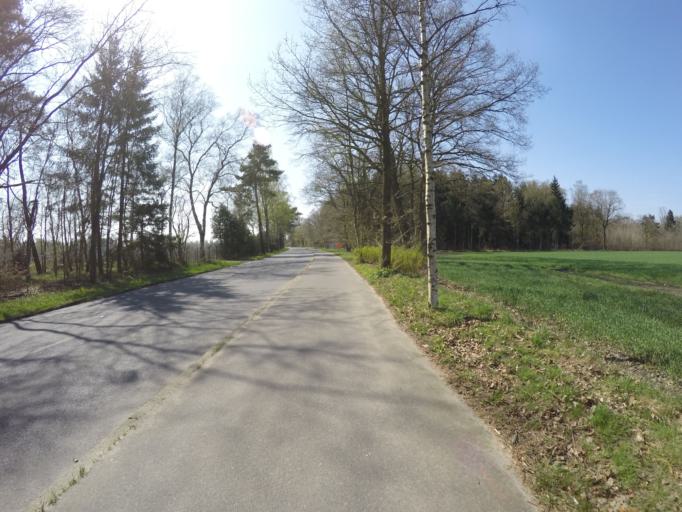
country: DE
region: Schleswig-Holstein
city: Quickborn
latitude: 53.7301
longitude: 9.9333
